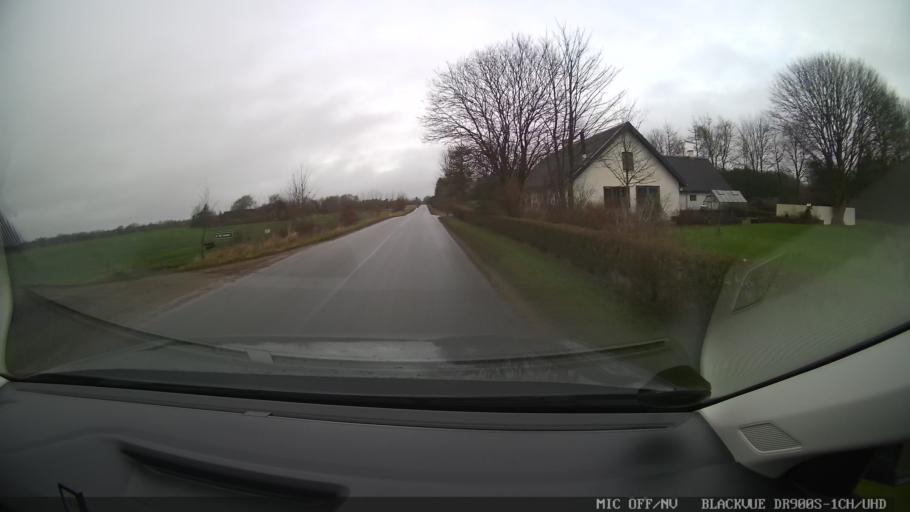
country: DK
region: Central Jutland
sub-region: Viborg Kommune
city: Karup
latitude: 56.3451
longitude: 9.2833
